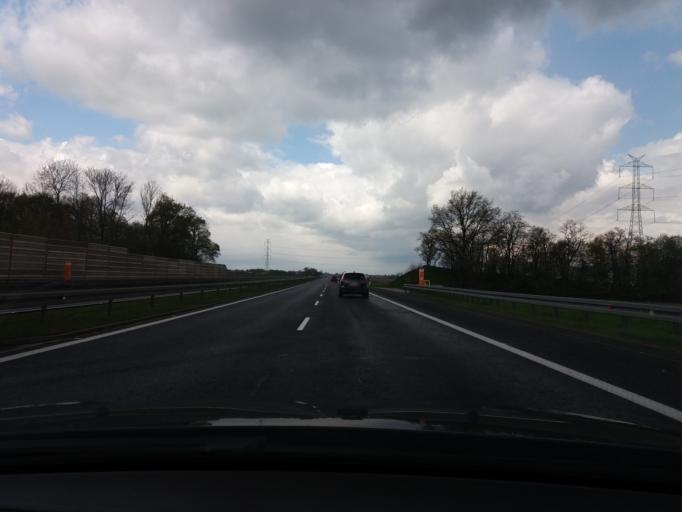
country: PL
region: Lower Silesian Voivodeship
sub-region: Powiat olawski
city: Wierzbno
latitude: 50.9369
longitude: 17.1086
